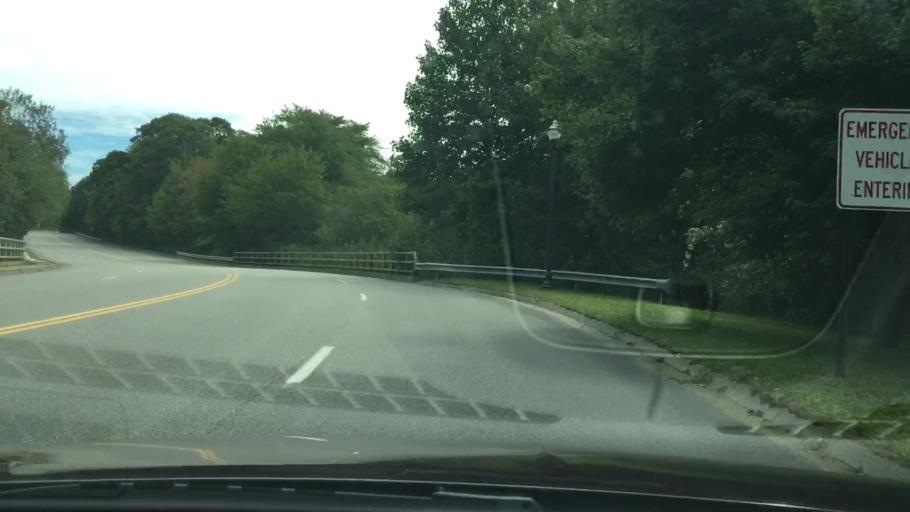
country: US
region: Connecticut
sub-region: Middlesex County
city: Westbrook Center
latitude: 41.2895
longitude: -72.4397
